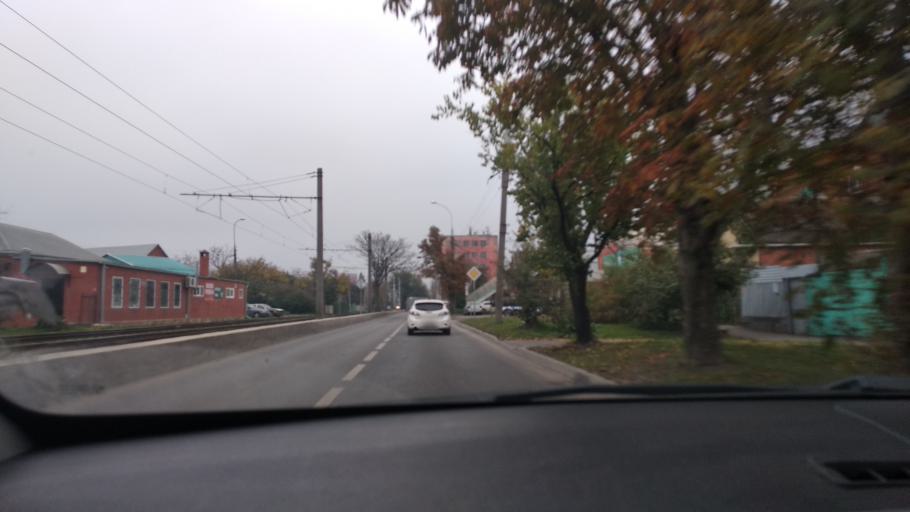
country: RU
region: Krasnodarskiy
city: Krasnodar
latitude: 45.0103
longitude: 39.0131
